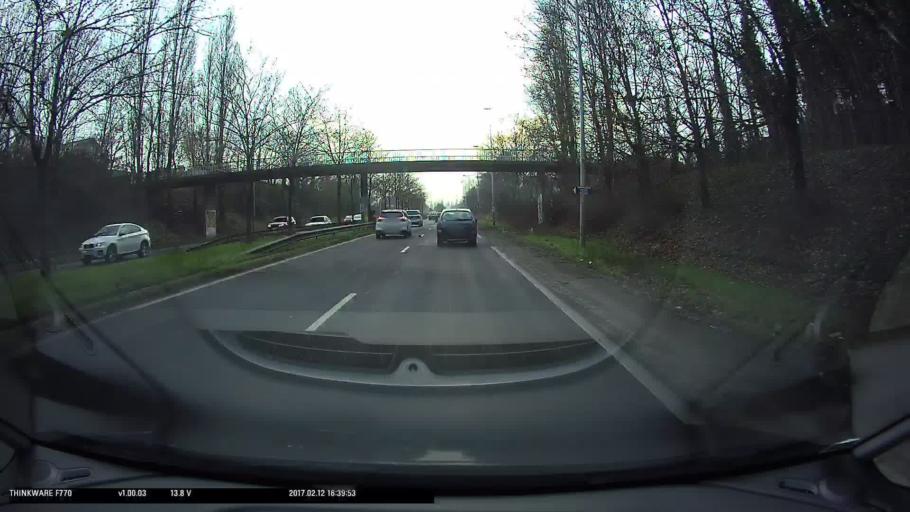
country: FR
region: Ile-de-France
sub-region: Departement du Val-d'Oise
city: Eragny
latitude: 49.0200
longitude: 2.0984
